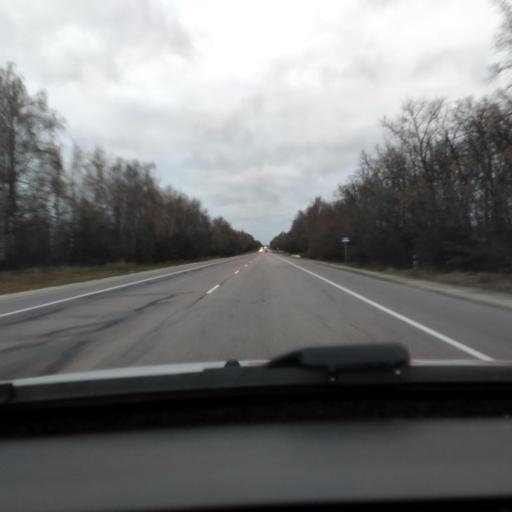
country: RU
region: Lipetsk
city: Khlevnoye
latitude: 52.2938
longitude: 39.1674
